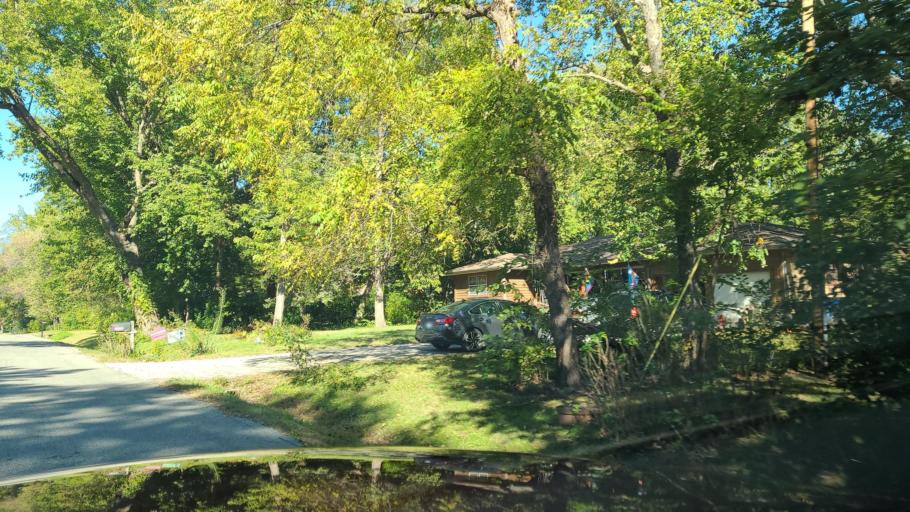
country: US
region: Kansas
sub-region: Douglas County
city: Lawrence
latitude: 38.9550
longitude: -95.2306
